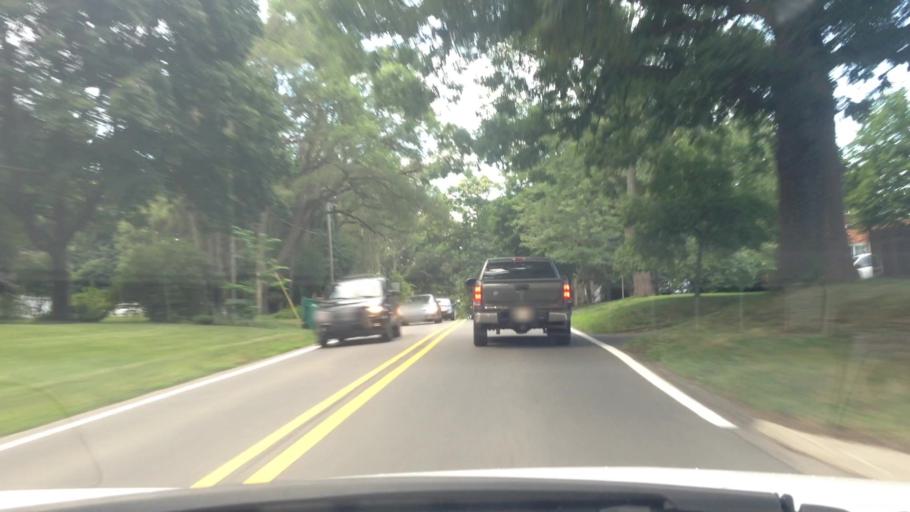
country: US
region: Michigan
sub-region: Oakland County
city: Pontiac
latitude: 42.6750
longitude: -83.3348
